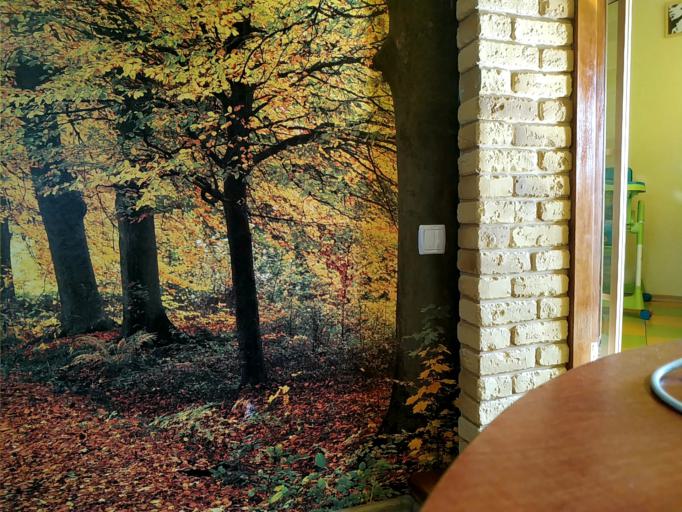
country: RU
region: Tverskaya
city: Kalashnikovo
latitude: 57.3423
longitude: 35.2576
